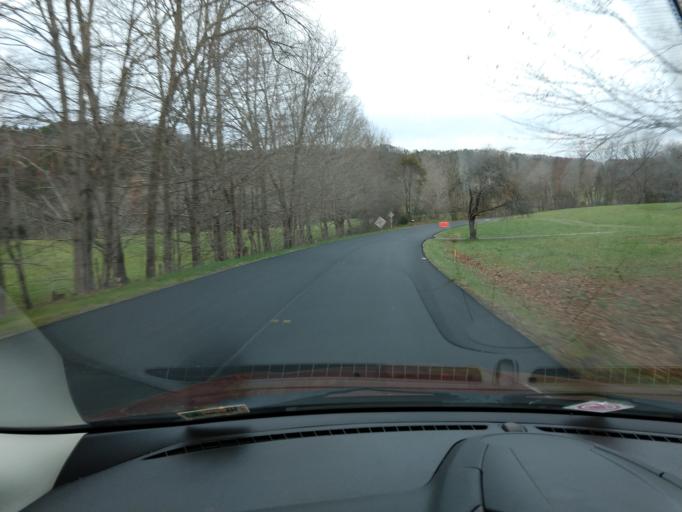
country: US
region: West Virginia
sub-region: Greenbrier County
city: White Sulphur Springs
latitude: 37.7366
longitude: -80.1906
